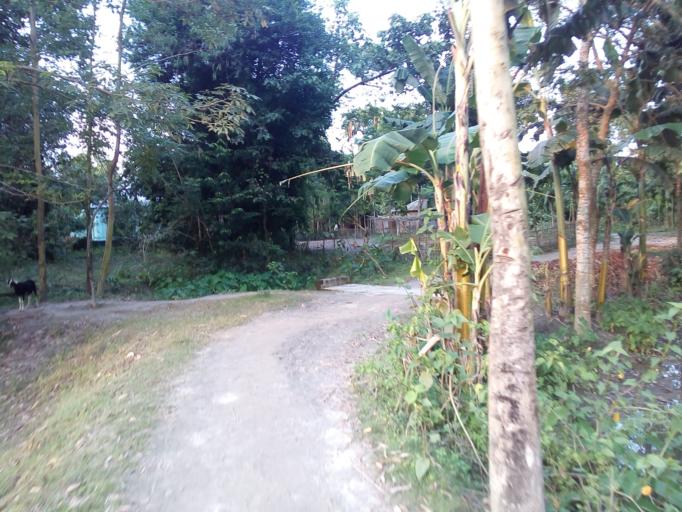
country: BD
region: Rangpur Division
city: Nageswari
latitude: 25.8699
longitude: 89.7855
